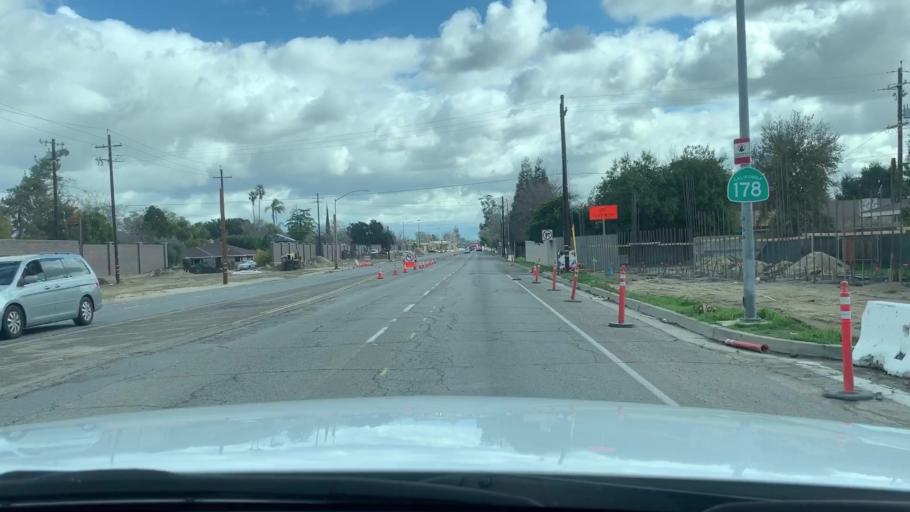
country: US
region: California
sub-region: Kern County
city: Bakersfield
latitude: 35.3810
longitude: -119.0350
